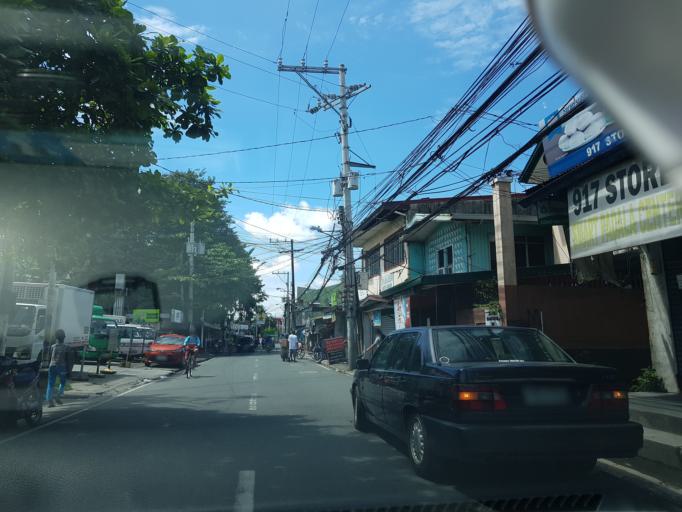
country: PH
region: Calabarzon
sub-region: Province of Rizal
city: Pateros
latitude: 14.5376
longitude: 121.0675
